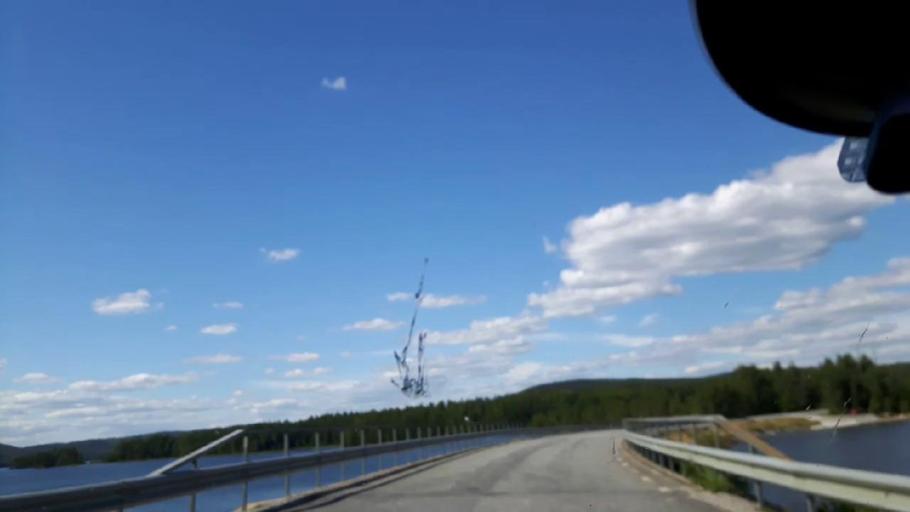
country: SE
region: Vaesternorrland
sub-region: Ange Kommun
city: Fransta
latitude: 62.6937
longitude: 16.3913
